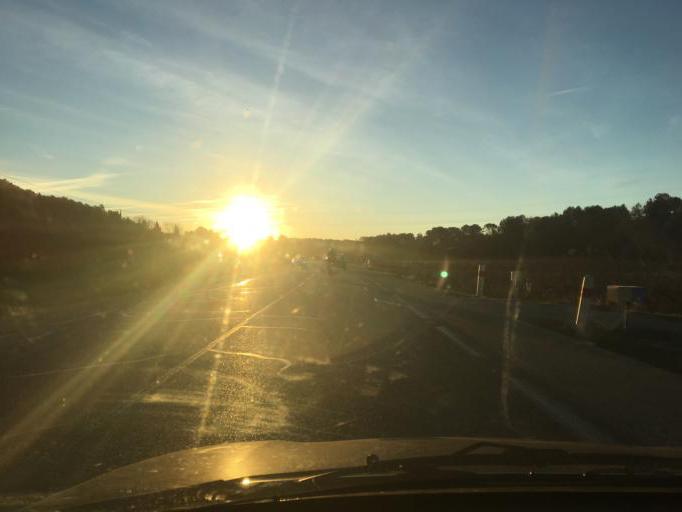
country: FR
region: Provence-Alpes-Cote d'Azur
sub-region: Departement du Var
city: Lorgues
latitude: 43.4700
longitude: 6.3823
